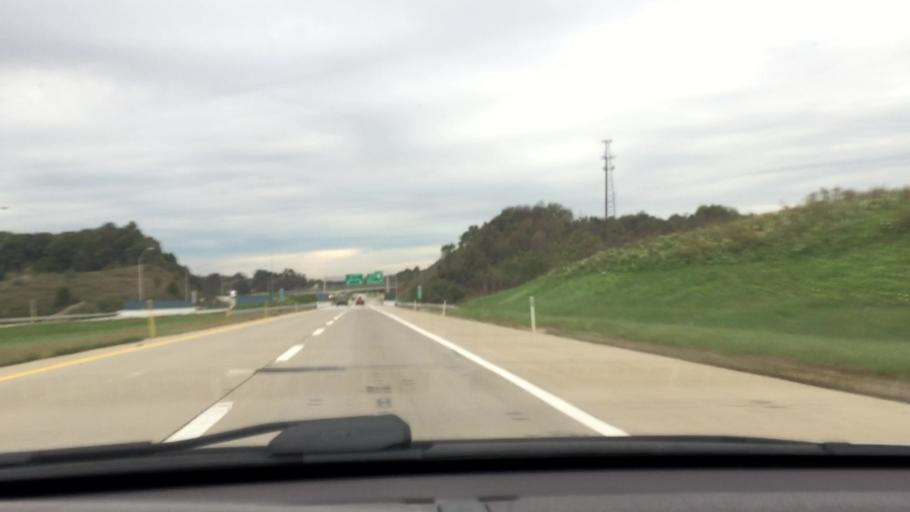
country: US
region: Pennsylvania
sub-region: Beaver County
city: Big Beaver
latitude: 40.8326
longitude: -80.3701
